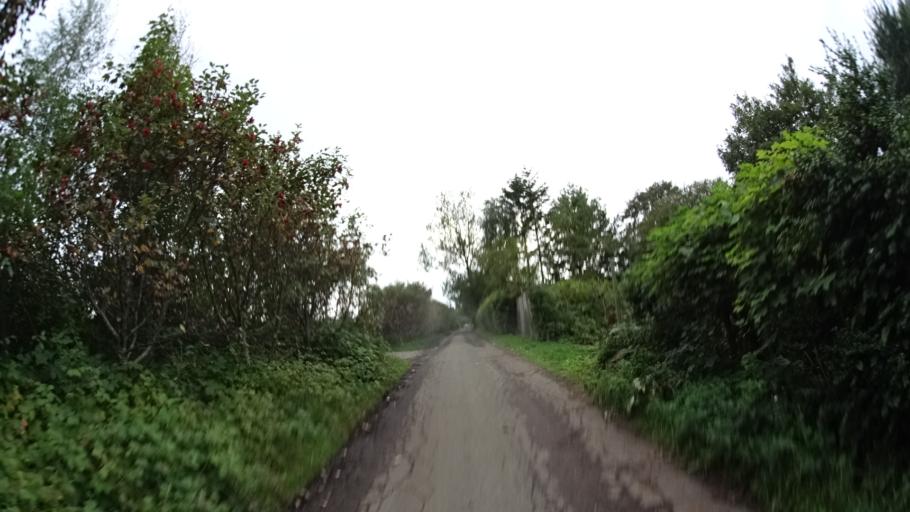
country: DK
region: Central Jutland
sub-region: Arhus Kommune
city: Arhus
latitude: 56.1476
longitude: 10.1778
